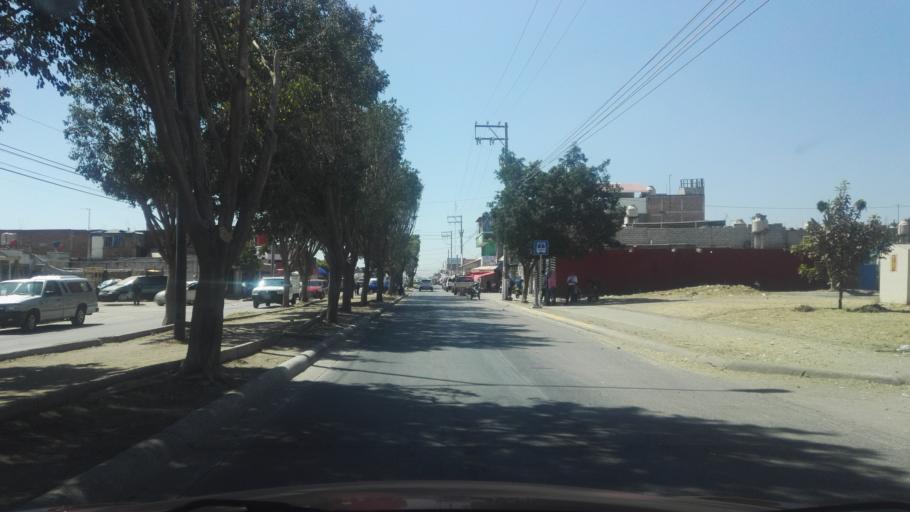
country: MX
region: Guanajuato
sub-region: Leon
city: Fraccionamiento Paraiso Real
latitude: 21.0962
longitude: -101.5901
